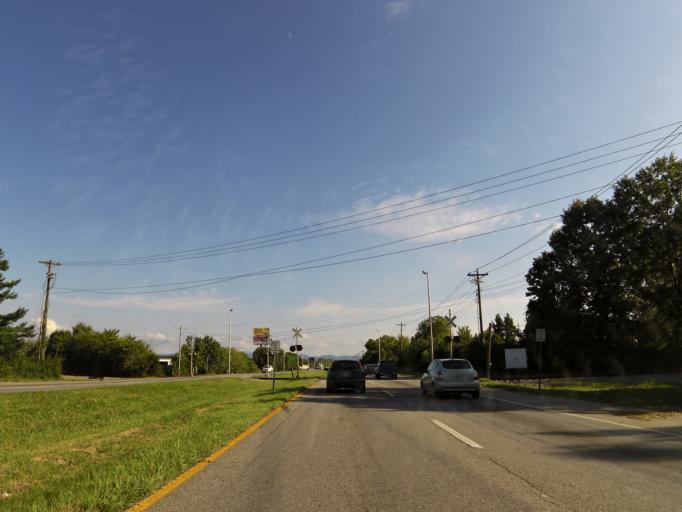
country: US
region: Tennessee
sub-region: Blount County
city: Alcoa
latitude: 35.7777
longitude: -83.9898
